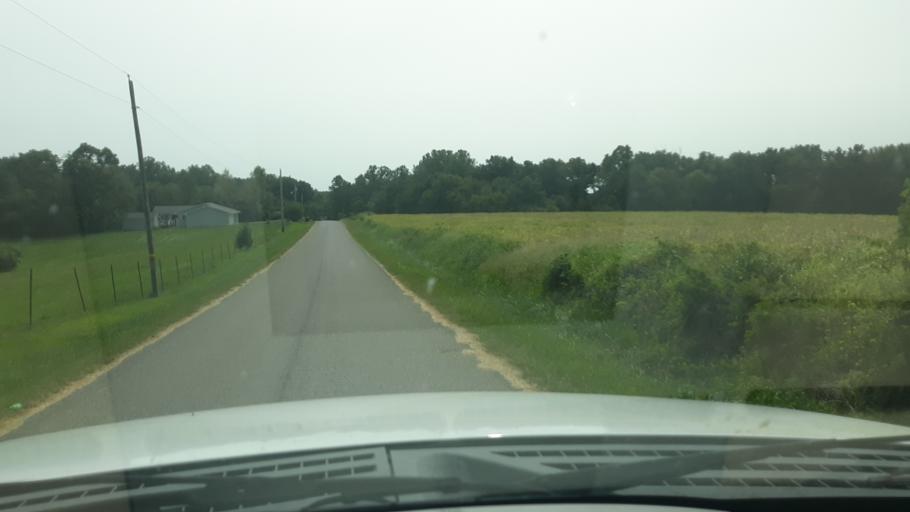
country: US
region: Illinois
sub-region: Saline County
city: Eldorado
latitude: 37.8405
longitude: -88.5004
